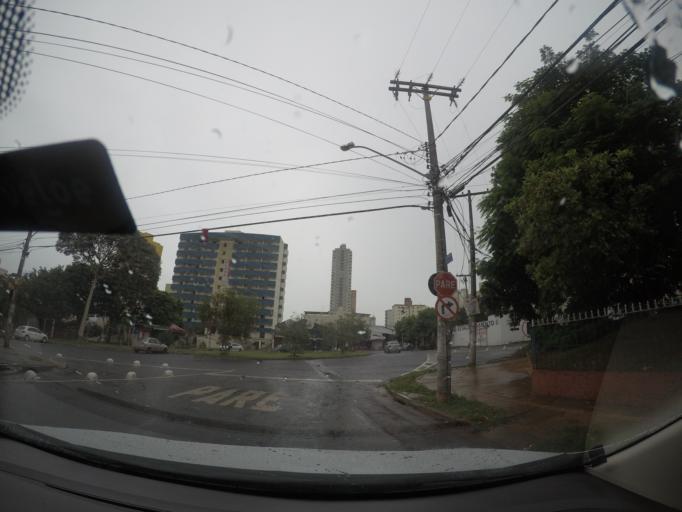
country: BR
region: Goias
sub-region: Goiania
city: Goiania
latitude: -16.6757
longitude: -49.2476
